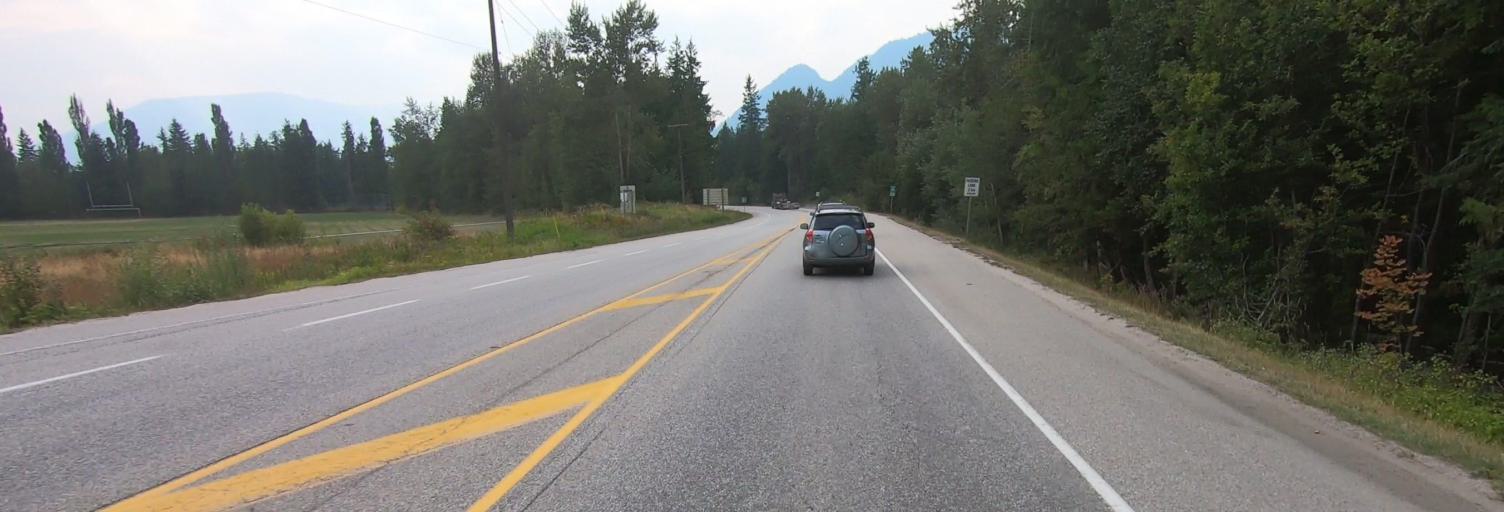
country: CA
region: British Columbia
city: Sicamous
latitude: 50.8387
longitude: -118.9781
